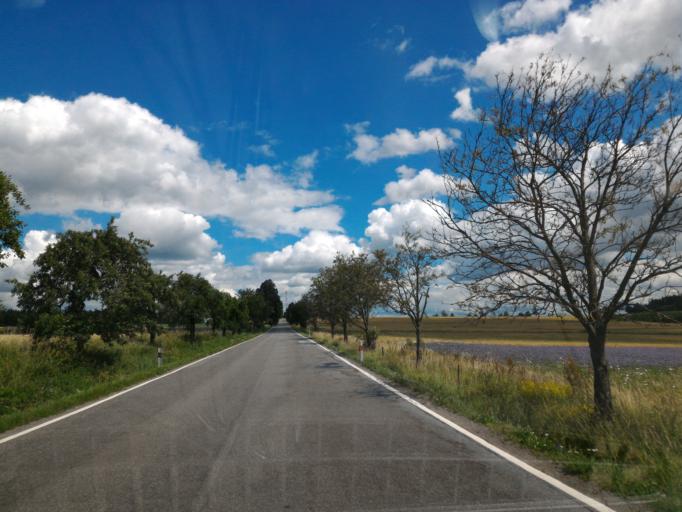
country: CZ
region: Vysocina
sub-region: Okres Jihlava
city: Polna
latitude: 49.4384
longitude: 15.7322
